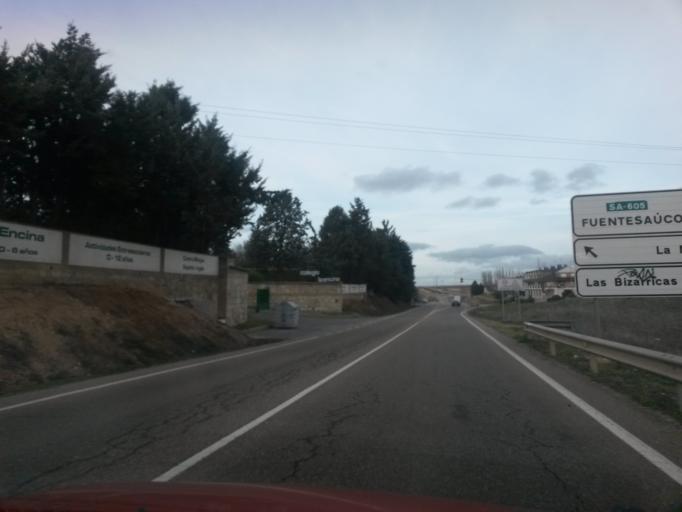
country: ES
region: Castille and Leon
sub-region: Provincia de Salamanca
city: Villares de la Reina
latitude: 40.9921
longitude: -5.6582
